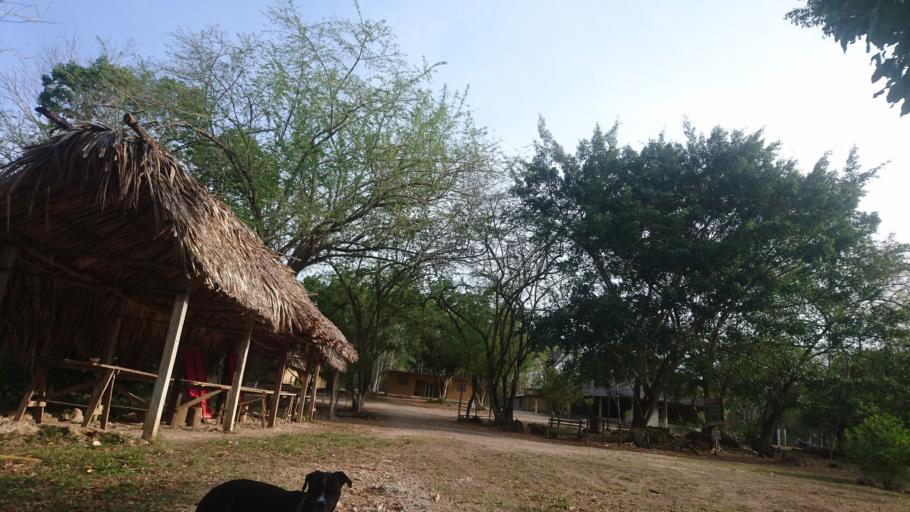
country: MX
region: Chiapas
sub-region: Ocosingo
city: Frontera Corozal
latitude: 16.8232
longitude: -90.8855
